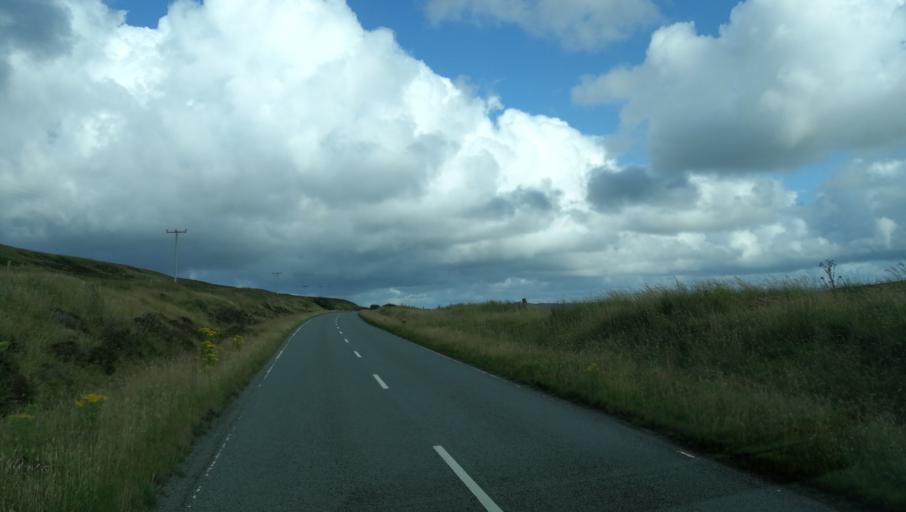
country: GB
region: Scotland
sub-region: Highland
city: Isle of Skye
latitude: 57.4679
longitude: -6.5190
